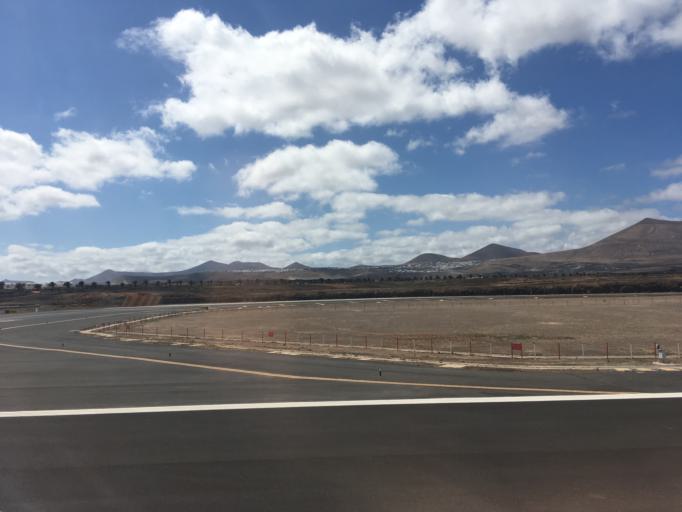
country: ES
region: Canary Islands
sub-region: Provincia de Las Palmas
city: Tias
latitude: 28.9364
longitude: -13.6105
